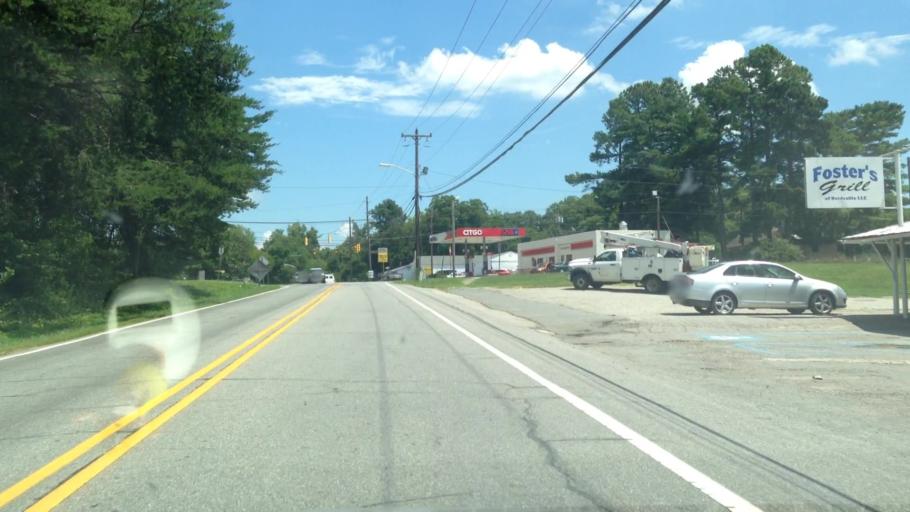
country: US
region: North Carolina
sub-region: Rockingham County
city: Reidsville
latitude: 36.3555
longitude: -79.6795
